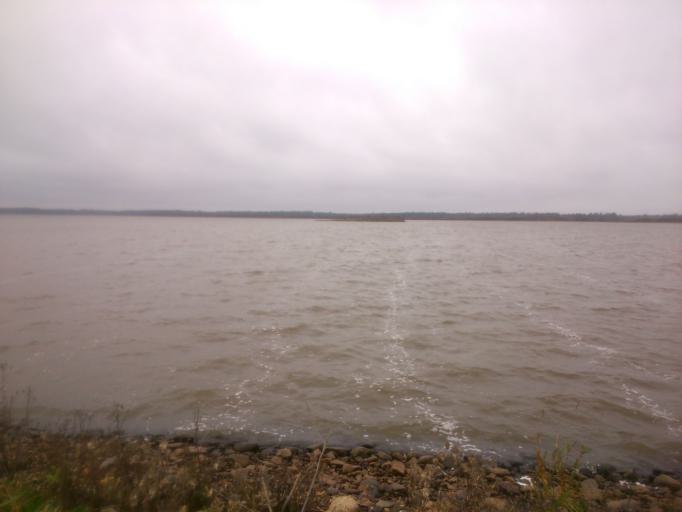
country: DK
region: South Denmark
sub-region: Varde Kommune
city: Oksbol
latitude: 55.6994
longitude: 8.2114
